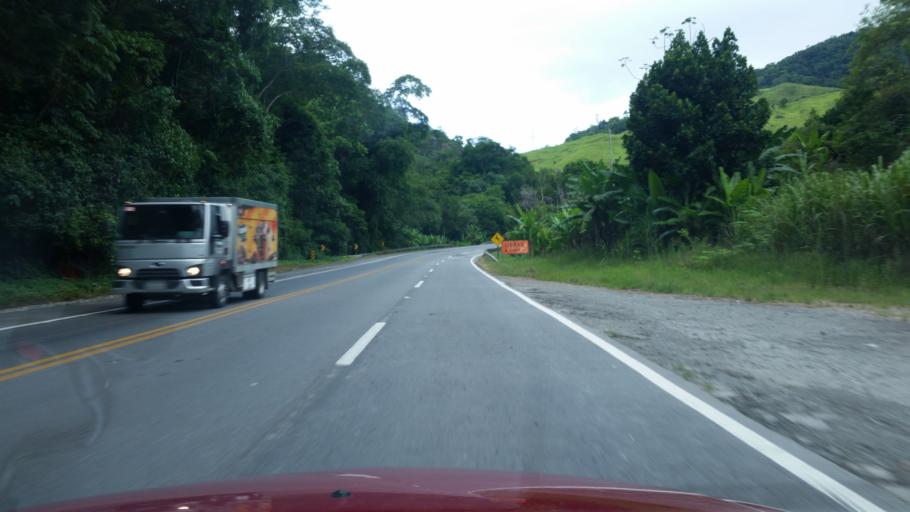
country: BR
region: Sao Paulo
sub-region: Miracatu
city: Miracatu
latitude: -24.2665
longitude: -47.2924
